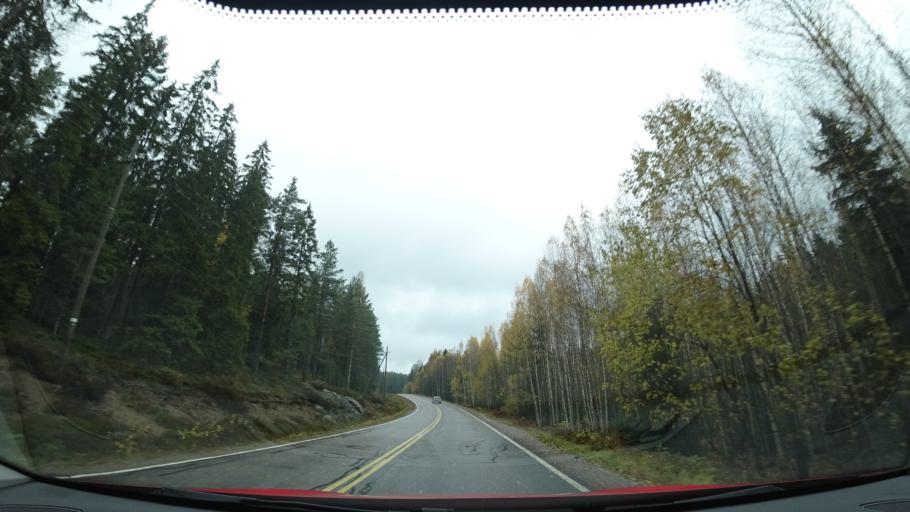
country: FI
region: Uusimaa
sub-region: Helsinki
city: Sibbo
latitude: 60.2860
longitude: 25.1967
